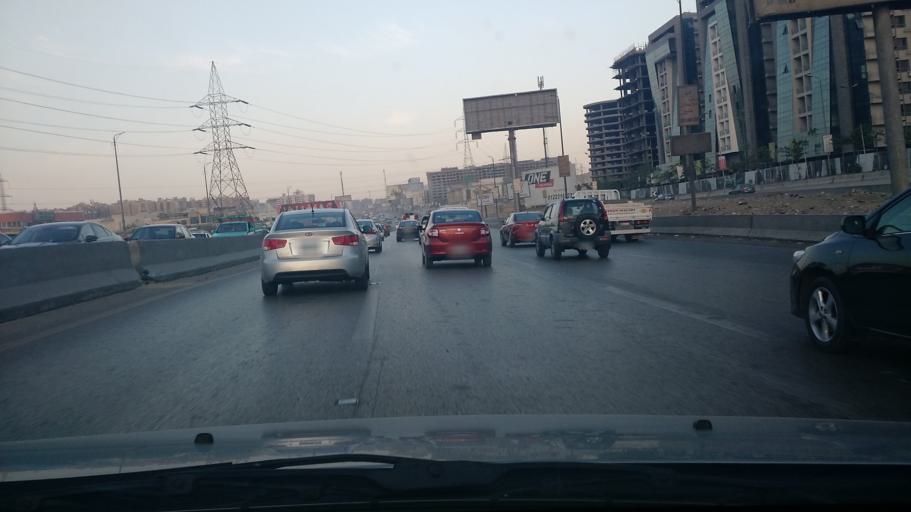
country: EG
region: Muhafazat al Qahirah
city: Cairo
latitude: 29.9842
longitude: 31.3225
